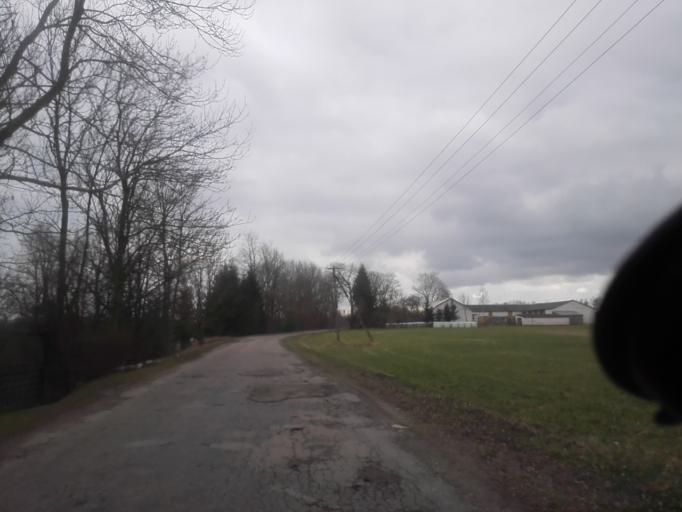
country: PL
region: Podlasie
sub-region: Suwalki
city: Suwalki
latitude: 54.2532
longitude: 22.9996
